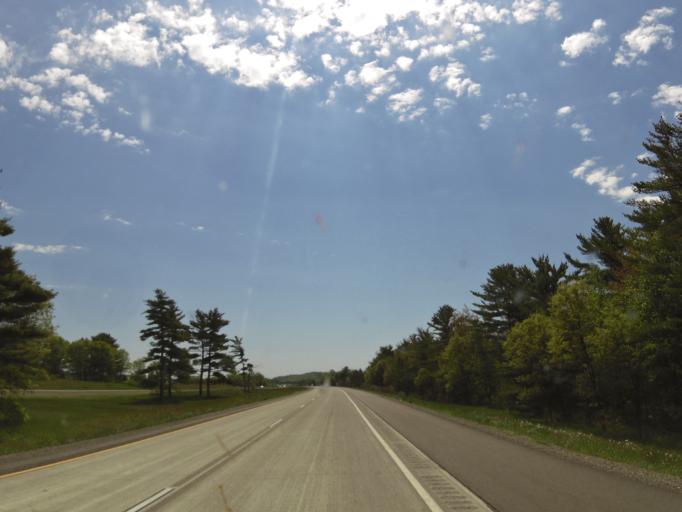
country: US
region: Wisconsin
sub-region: Jackson County
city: Black River Falls
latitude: 44.3674
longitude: -90.9731
